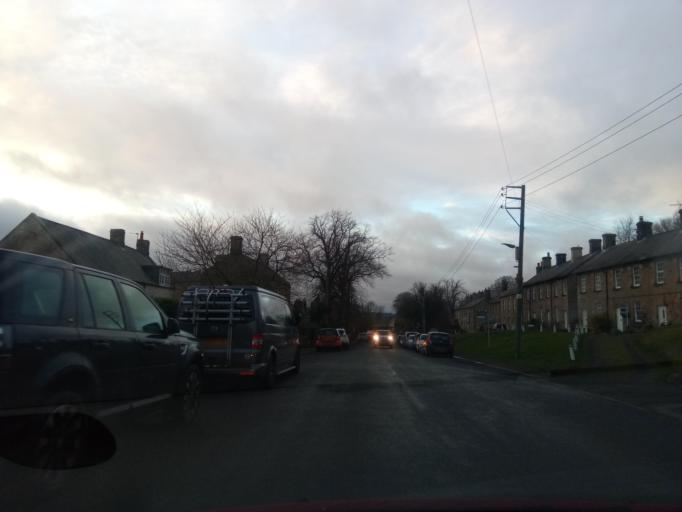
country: GB
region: England
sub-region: Northumberland
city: Meldon
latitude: 55.1270
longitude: -1.7968
